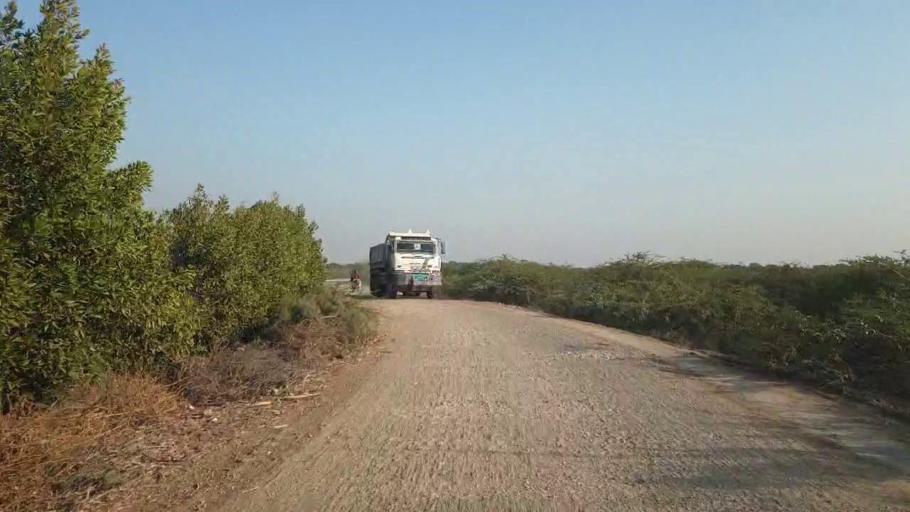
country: PK
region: Sindh
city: Mirpur Khas
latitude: 25.4229
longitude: 68.9057
